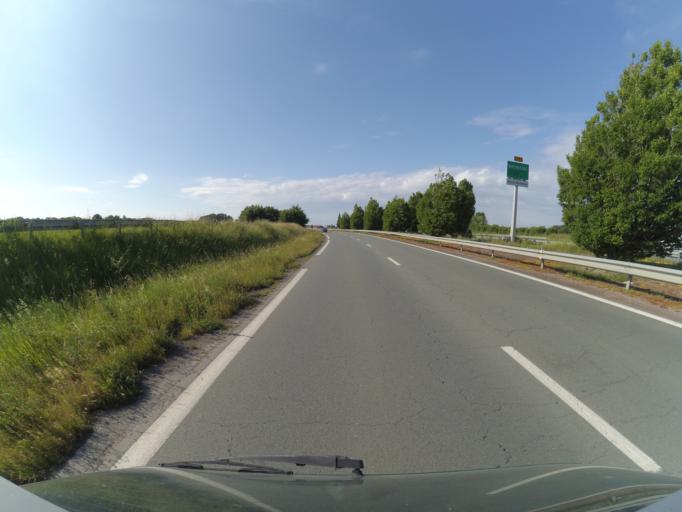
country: FR
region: Poitou-Charentes
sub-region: Departement de la Charente-Maritime
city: Saint-Agnant
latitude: 45.8864
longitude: -0.9607
